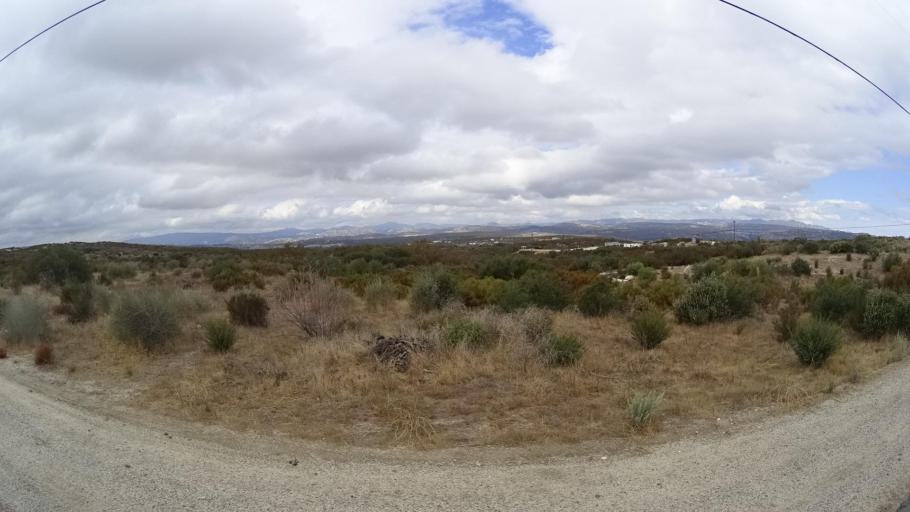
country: US
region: California
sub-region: San Diego County
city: Campo
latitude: 32.6446
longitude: -116.3182
